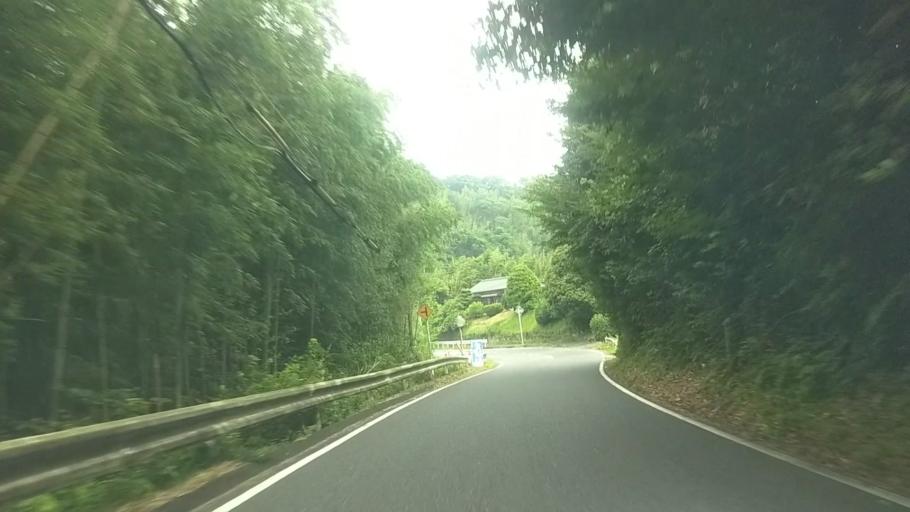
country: JP
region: Chiba
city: Kimitsu
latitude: 35.2478
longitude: 139.9922
